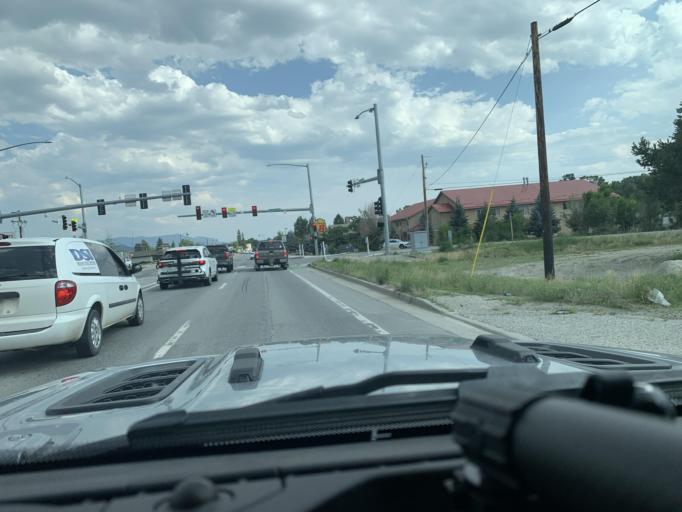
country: US
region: Colorado
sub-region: Chaffee County
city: Buena Vista
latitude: 38.8474
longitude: -106.1359
